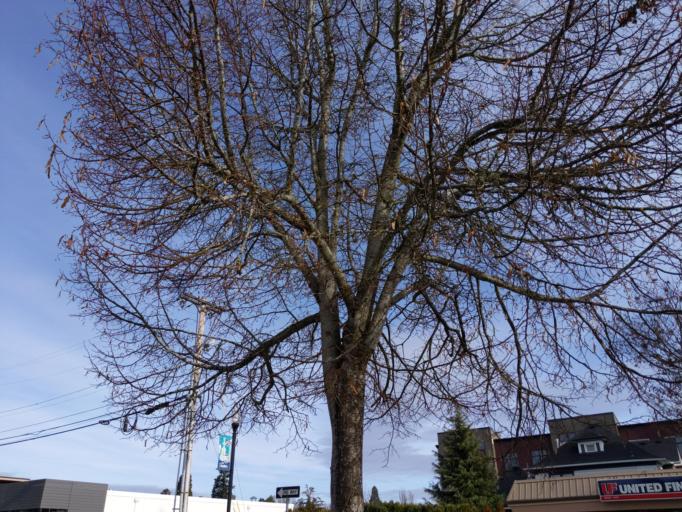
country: US
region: Oregon
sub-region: Washington County
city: Hillsboro
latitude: 45.5215
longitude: -122.9845
